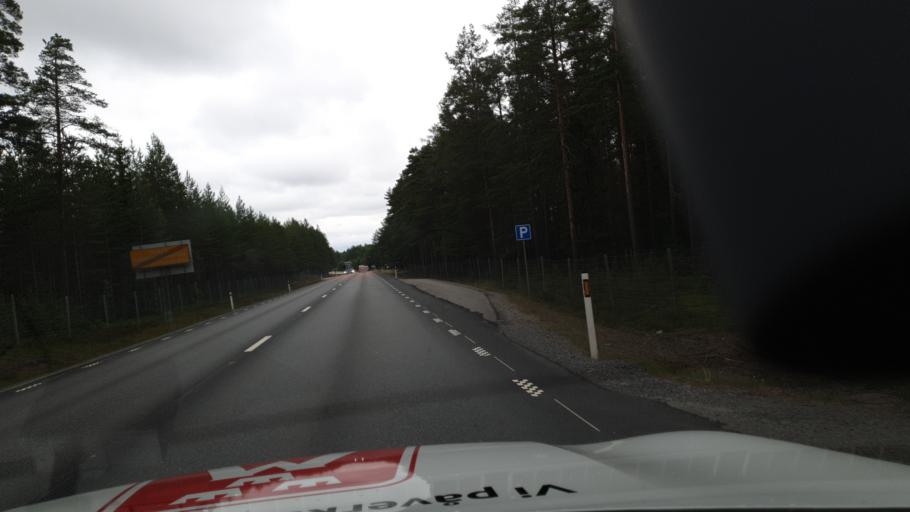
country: SE
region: Vaesterbotten
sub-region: Skelleftea Kommun
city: Burea
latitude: 64.5980
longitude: 21.2069
